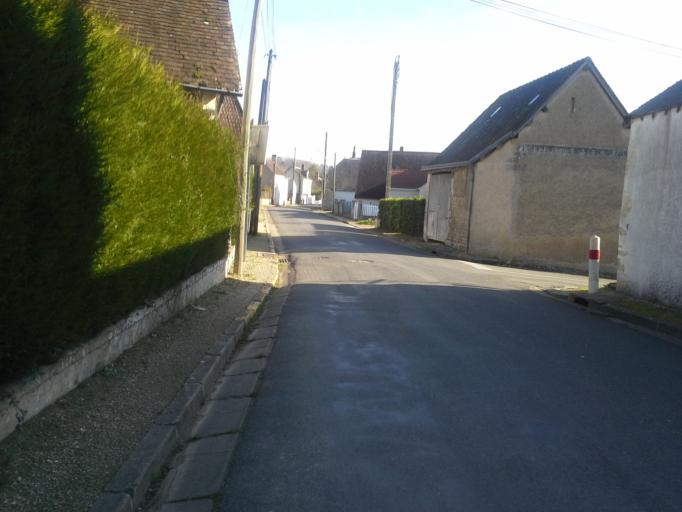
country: FR
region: Centre
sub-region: Departement du Loir-et-Cher
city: Villiers-sur-Loir
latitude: 47.8088
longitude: 0.9867
